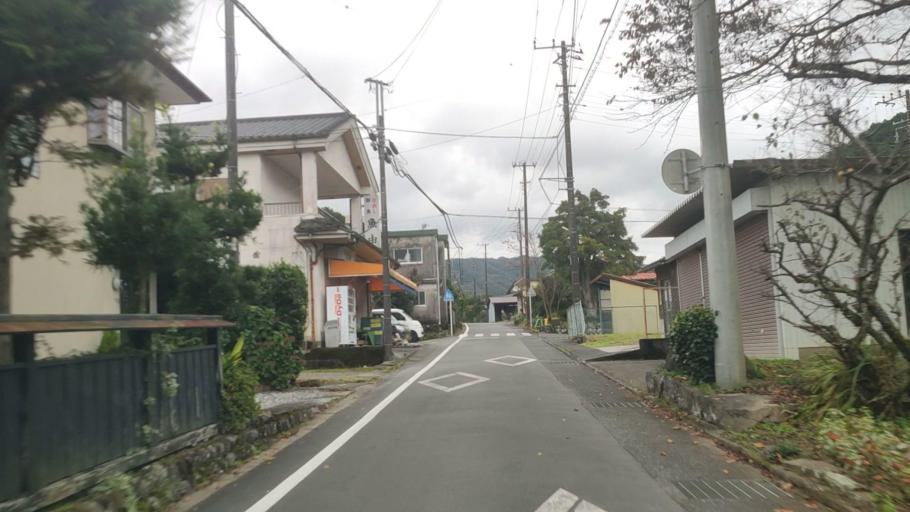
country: JP
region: Shizuoka
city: Ito
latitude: 34.9243
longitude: 138.9979
